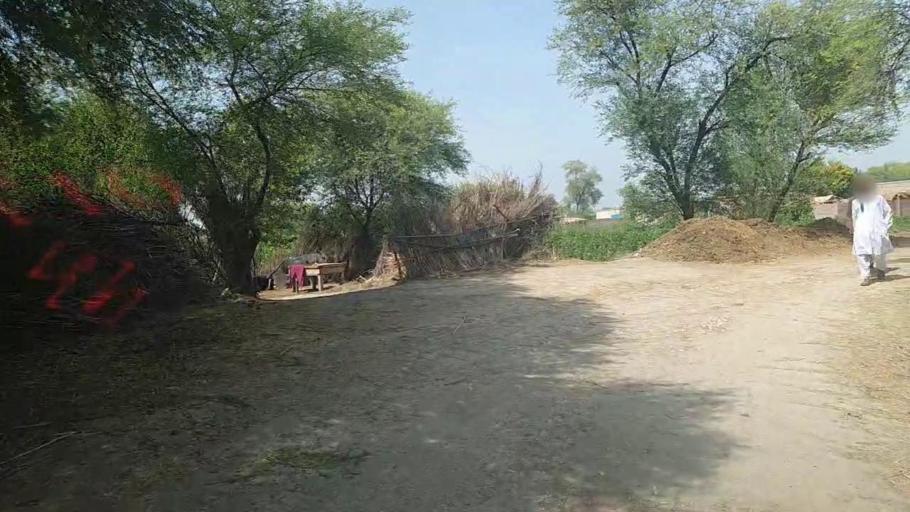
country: PK
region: Sindh
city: Ubauro
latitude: 28.1798
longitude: 69.8148
